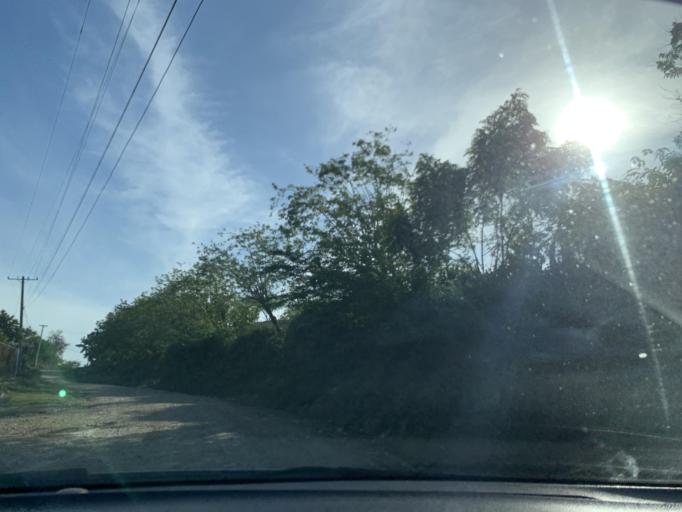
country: DO
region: Puerto Plata
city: Luperon
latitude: 19.8763
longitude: -70.9346
